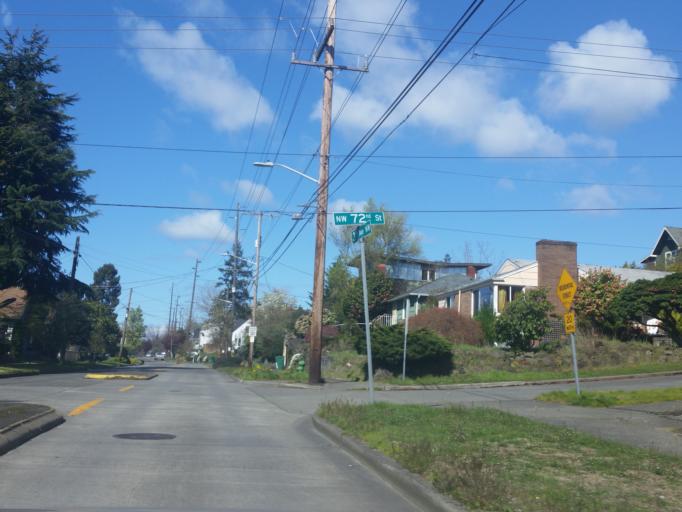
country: US
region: Washington
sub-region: King County
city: Shoreline
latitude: 47.6806
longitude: -122.3605
